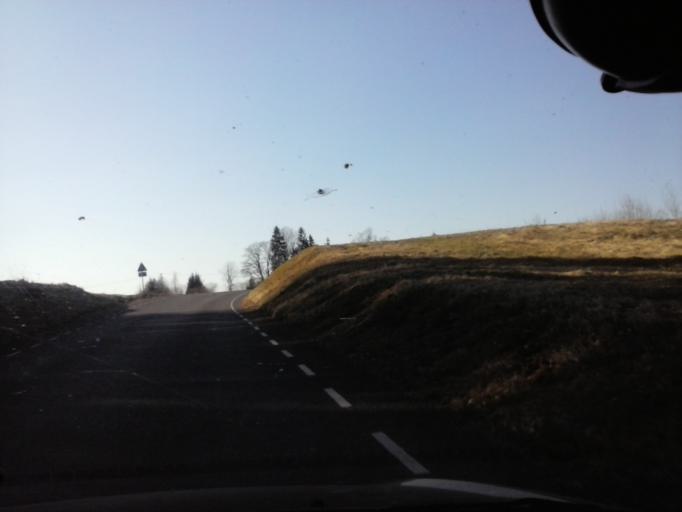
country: EE
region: Tartu
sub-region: UElenurme vald
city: Ulenurme
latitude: 58.1554
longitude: 26.8593
